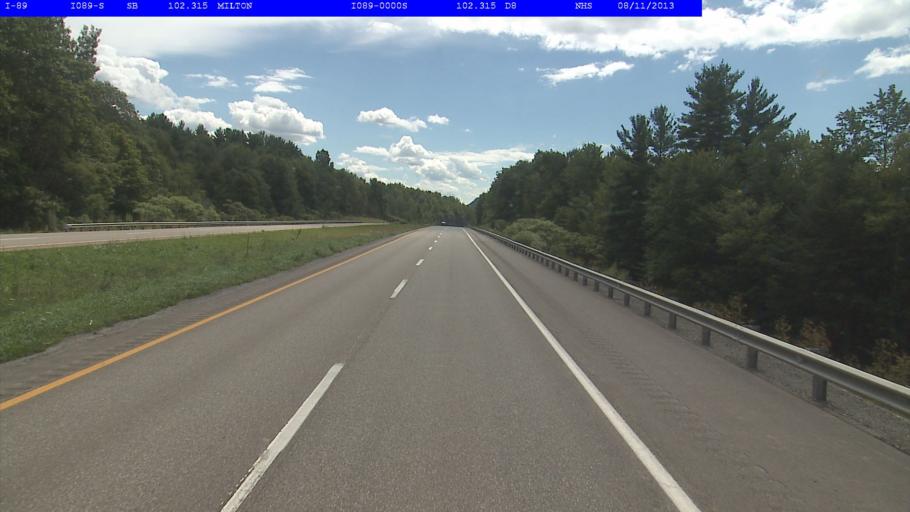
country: US
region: Vermont
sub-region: Chittenden County
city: Milton
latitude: 44.6469
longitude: -73.1403
